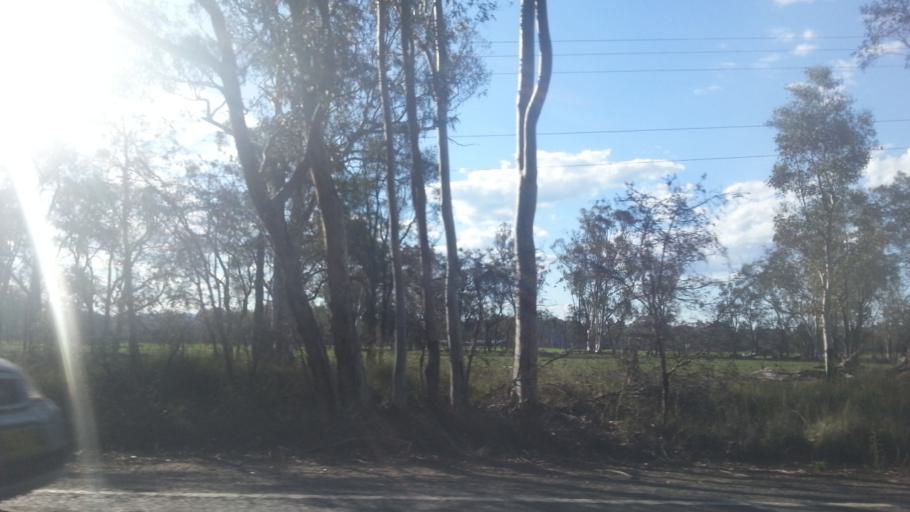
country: AU
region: New South Wales
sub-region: Penrith Municipality
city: Werrington Downs
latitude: -33.6771
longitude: 150.7455
